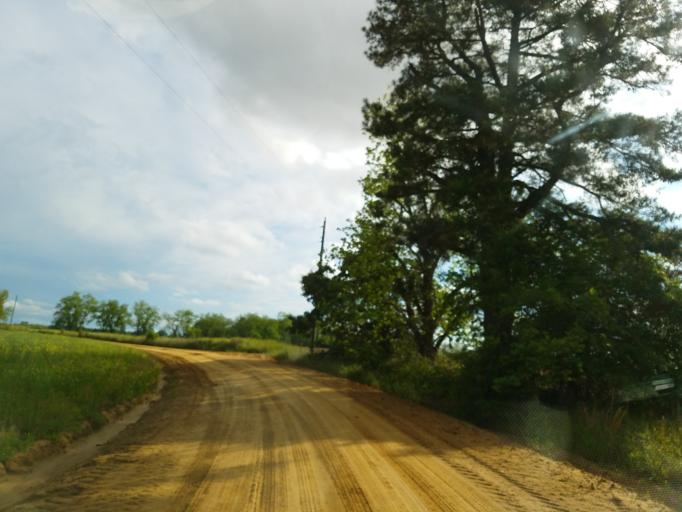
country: US
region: Georgia
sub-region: Dooly County
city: Unadilla
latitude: 32.1791
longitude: -83.7545
